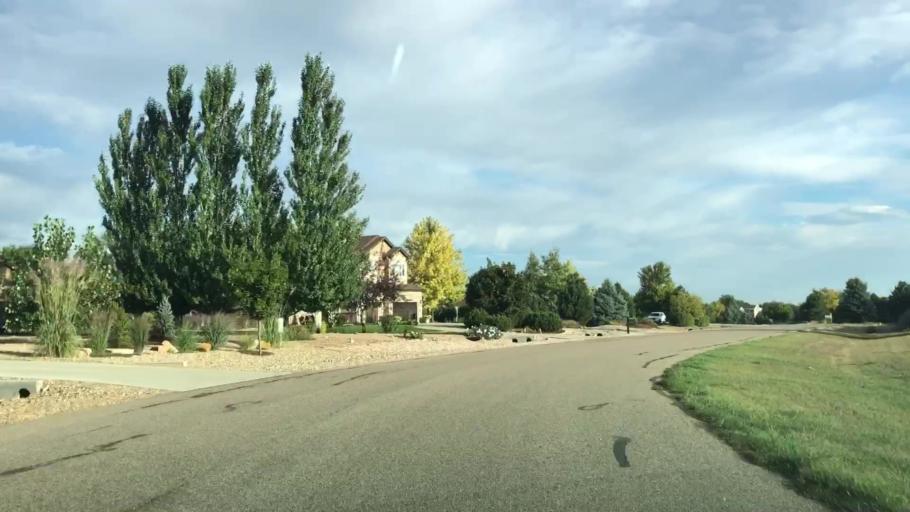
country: US
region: Colorado
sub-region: Weld County
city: Windsor
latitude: 40.4381
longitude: -104.9615
